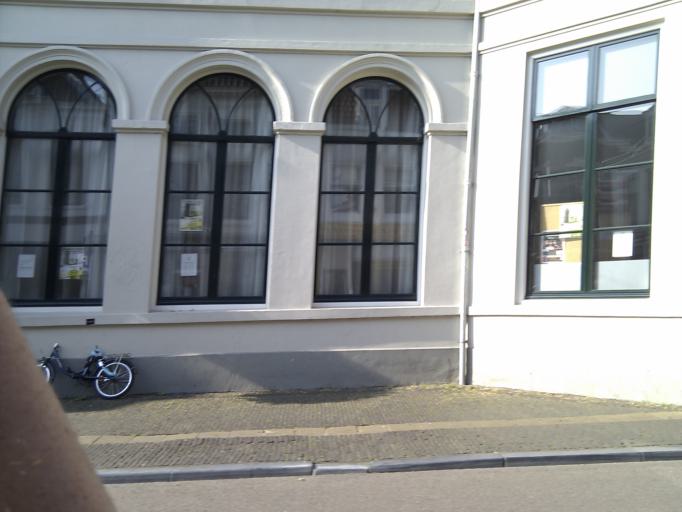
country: NL
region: Utrecht
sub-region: Gemeente Utrecht
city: Utrecht
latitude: 52.0951
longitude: 5.1244
